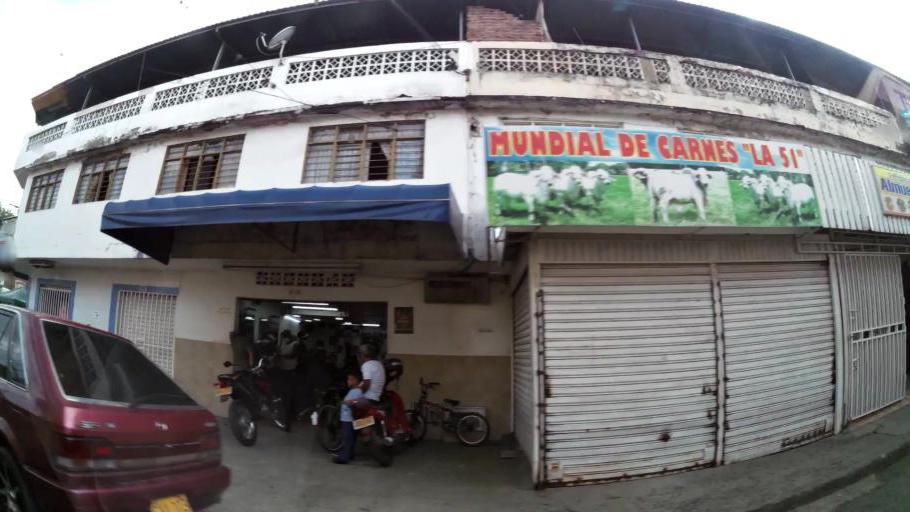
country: CO
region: Valle del Cauca
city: Cali
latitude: 3.4773
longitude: -76.5074
